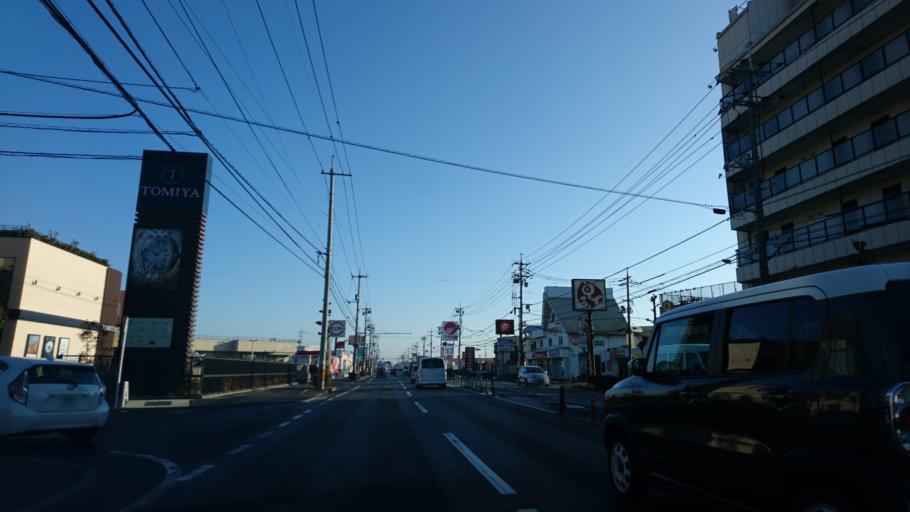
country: JP
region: Okayama
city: Kurashiki
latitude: 34.6110
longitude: 133.7646
